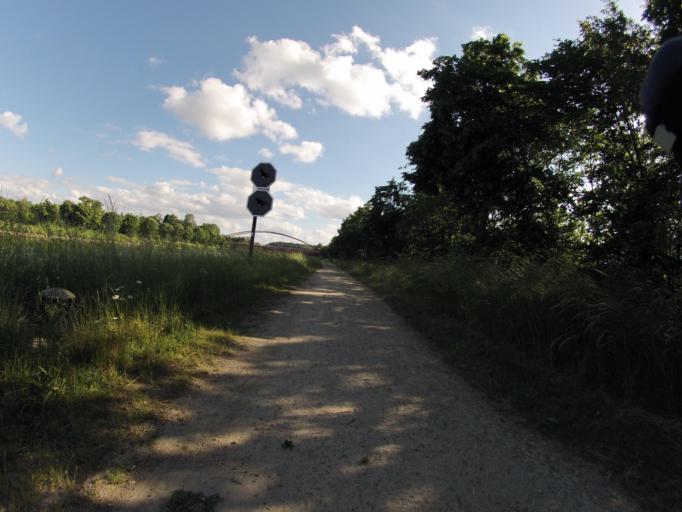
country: DE
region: North Rhine-Westphalia
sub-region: Regierungsbezirk Munster
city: Horstel
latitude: 52.2914
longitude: 7.6092
